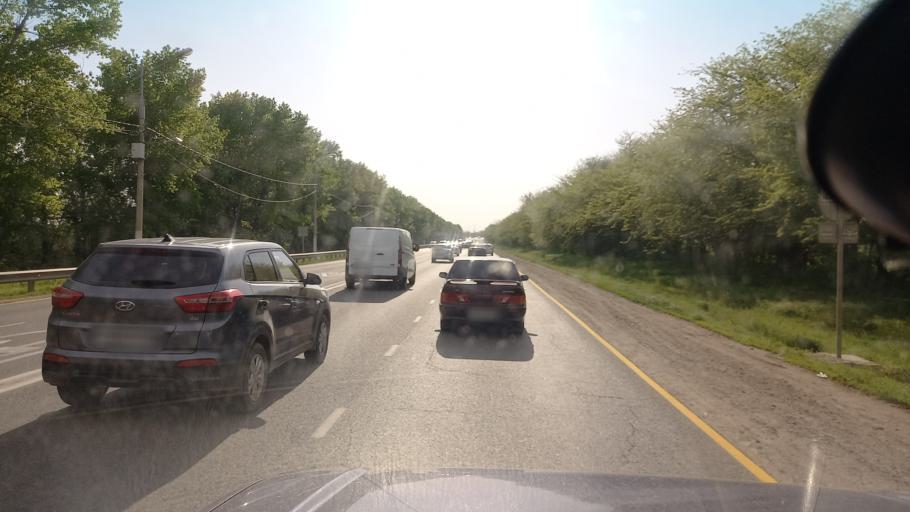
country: RU
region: Krasnodarskiy
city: Yelizavetinskaya
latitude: 45.0566
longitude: 38.8826
